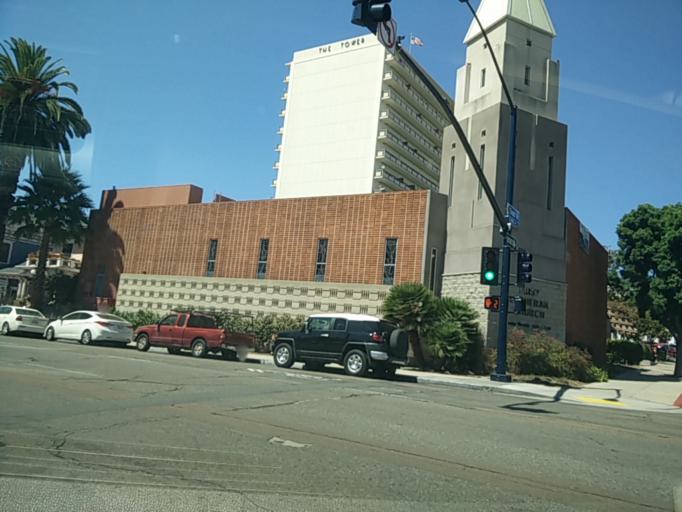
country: US
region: California
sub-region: San Diego County
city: San Diego
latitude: 32.7198
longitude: -117.1621
